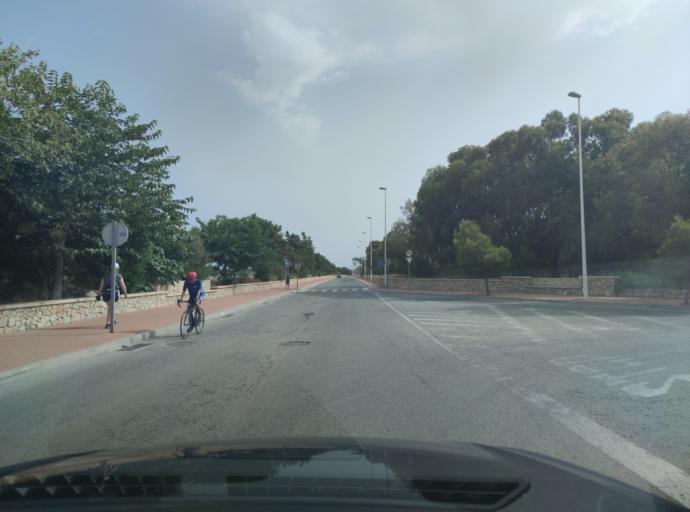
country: ES
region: Valencia
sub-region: Provincia de Alicante
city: Guardamar del Segura
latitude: 38.1046
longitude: -0.6549
